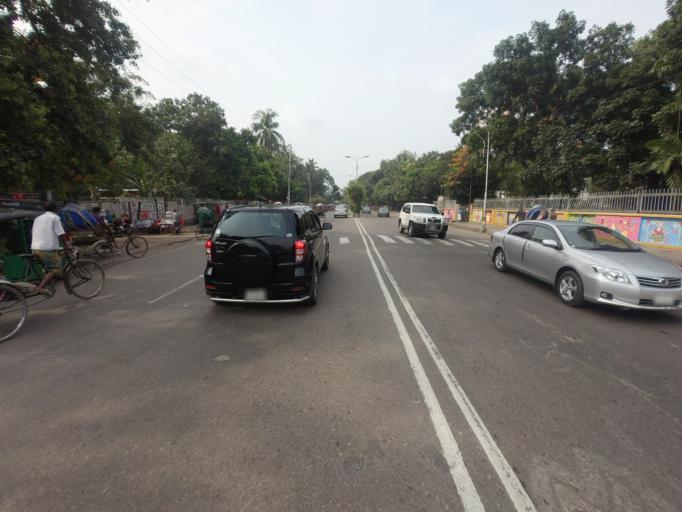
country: BD
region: Dhaka
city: Azimpur
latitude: 23.7356
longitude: 90.3953
